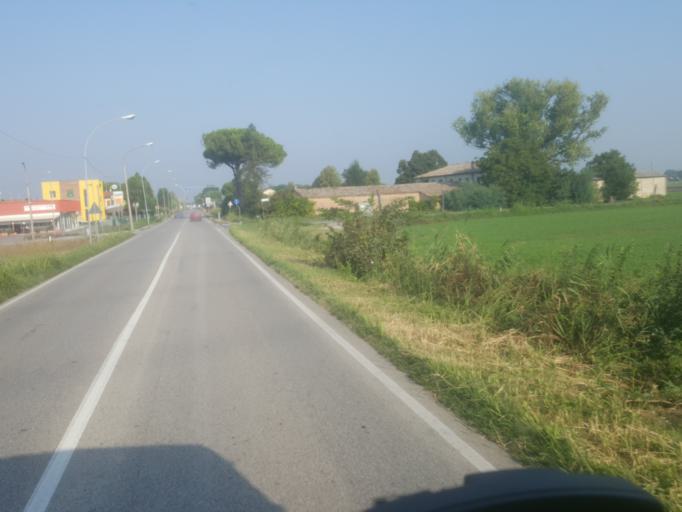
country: IT
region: Emilia-Romagna
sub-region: Provincia di Ravenna
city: Fornace Zarattini
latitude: 44.4469
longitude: 12.1271
